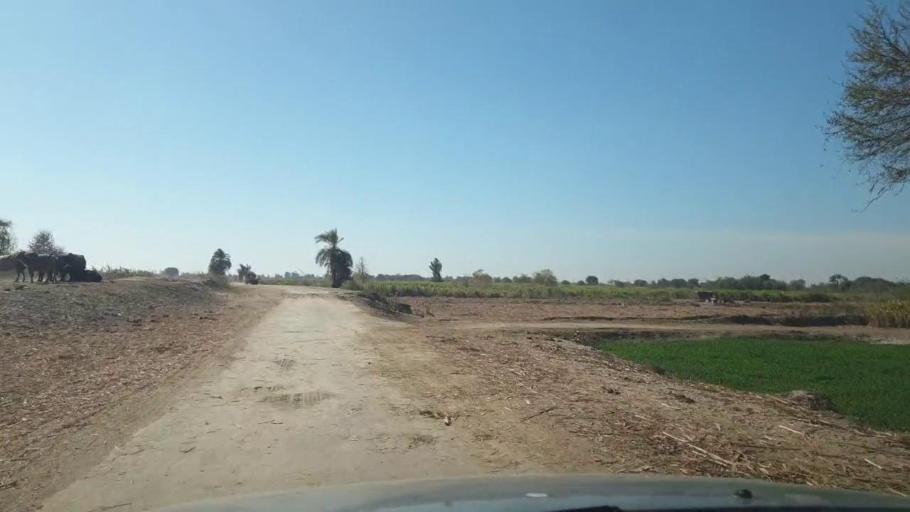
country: PK
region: Sindh
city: Ghotki
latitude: 28.0234
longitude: 69.2689
